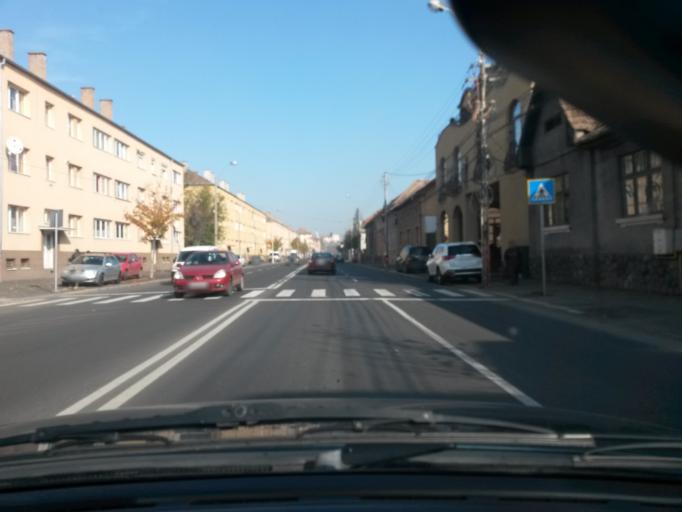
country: RO
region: Mures
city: Targu-Mures
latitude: 46.5335
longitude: 24.5525
